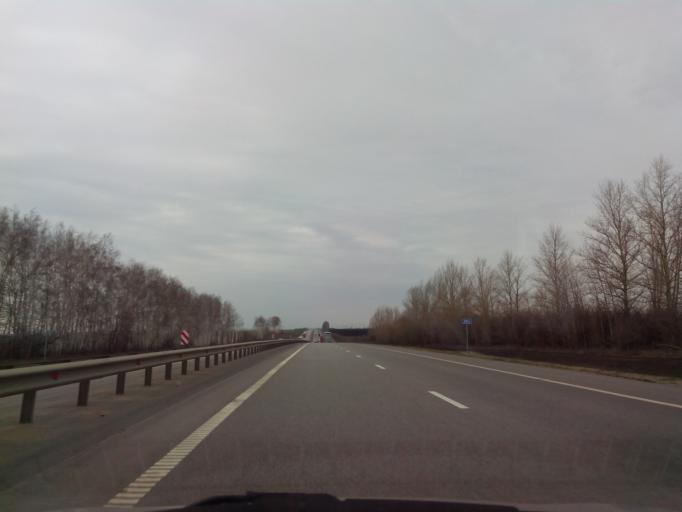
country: RU
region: Tambov
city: Selezni
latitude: 52.8113
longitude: 40.9533
